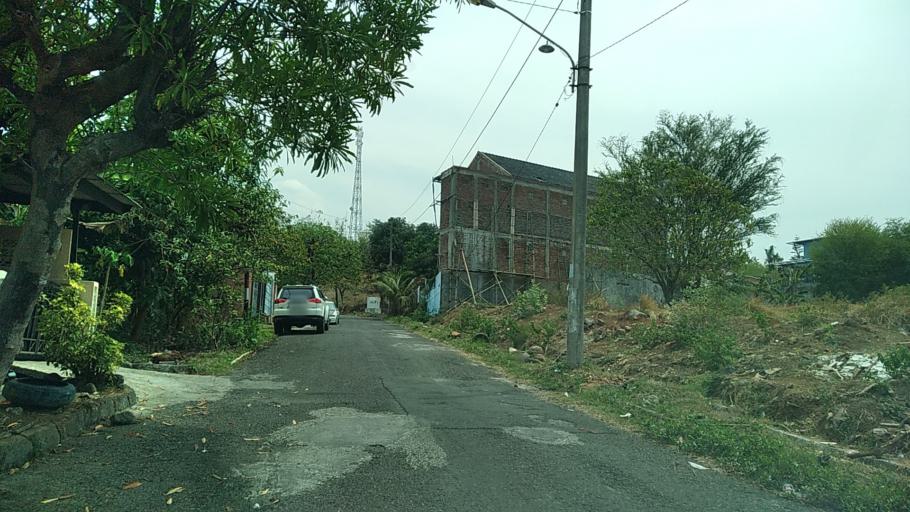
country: ID
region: Central Java
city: Semarang
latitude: -7.0417
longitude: 110.4420
